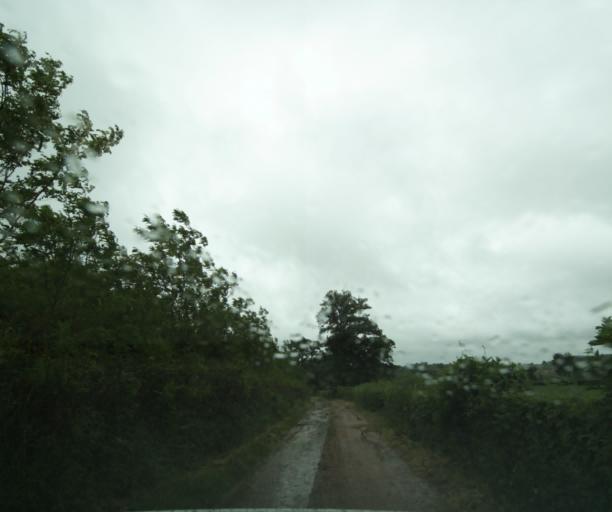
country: FR
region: Bourgogne
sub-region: Departement de Saone-et-Loire
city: Charolles
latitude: 46.4922
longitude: 4.4084
